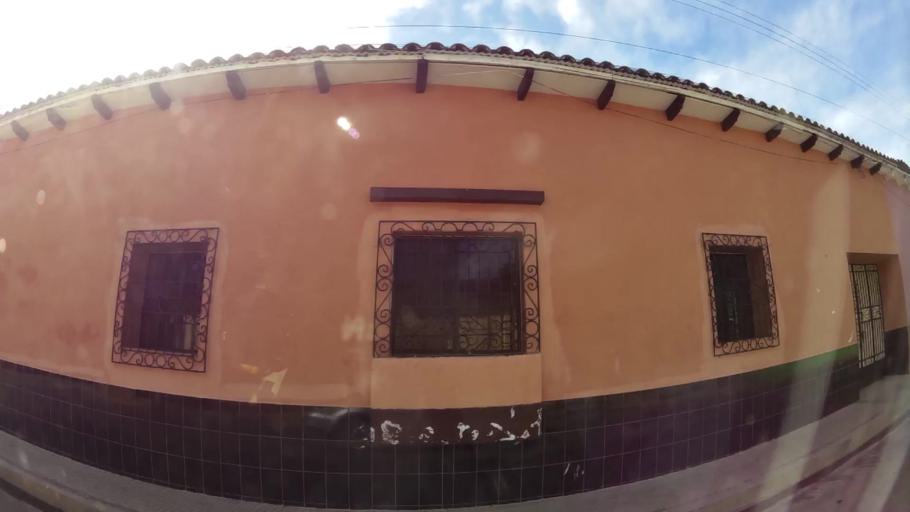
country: SV
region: Santa Ana
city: Chalchuapa
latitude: 13.9873
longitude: -89.6799
